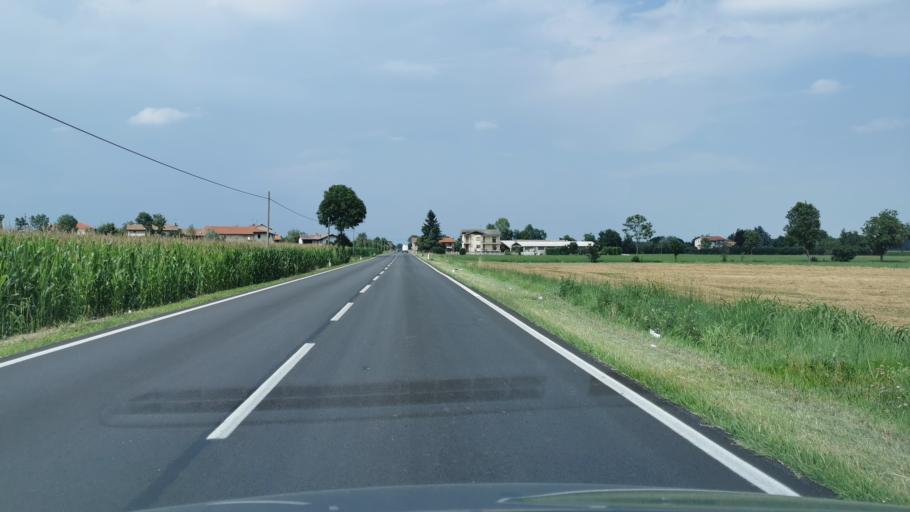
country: IT
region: Piedmont
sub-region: Provincia di Cuneo
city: Tarantasca
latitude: 44.4696
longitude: 7.5389
